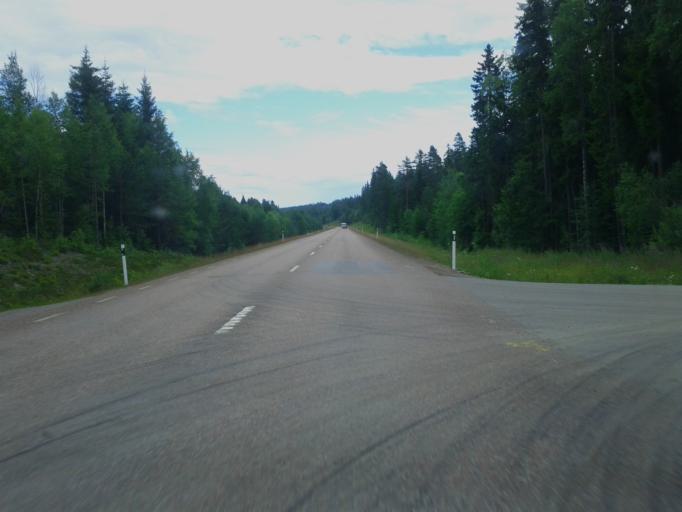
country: SE
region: Dalarna
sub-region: Faluns Kommun
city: Bjursas
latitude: 60.7543
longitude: 15.3435
